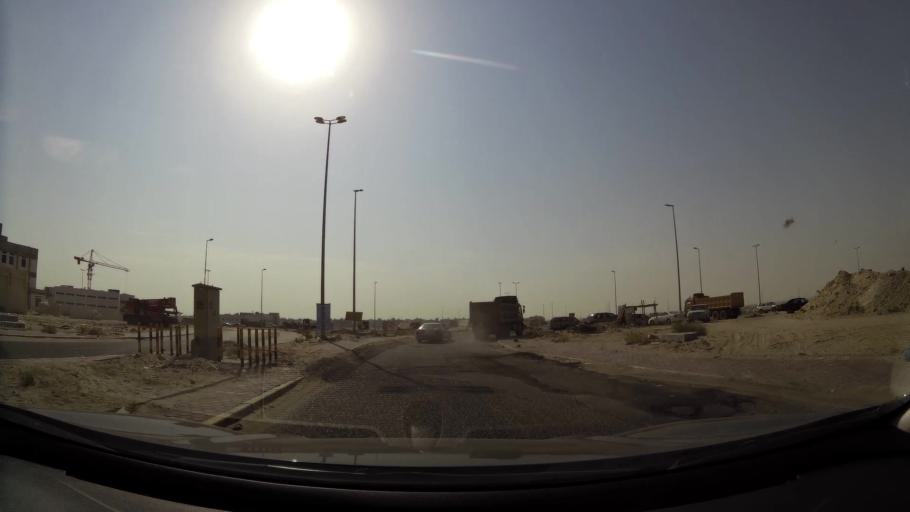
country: KW
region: Al Ahmadi
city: Al Wafrah
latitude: 28.7829
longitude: 48.0512
